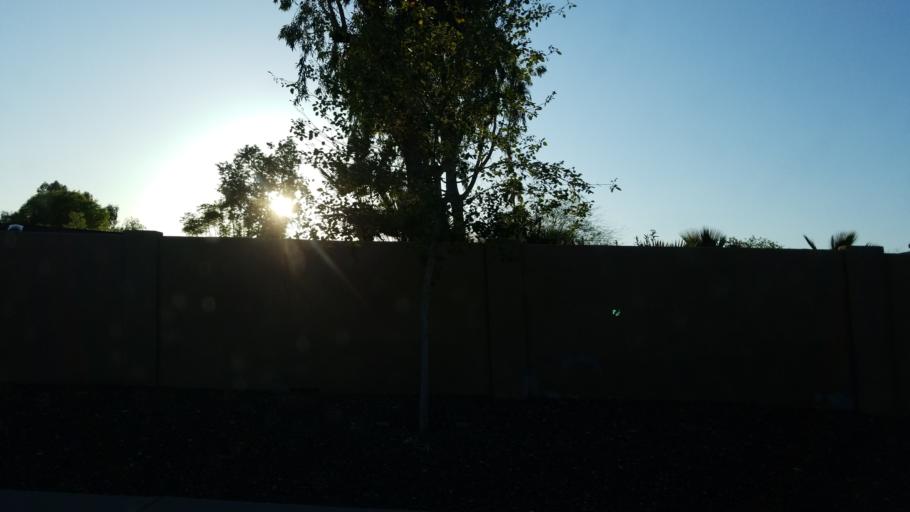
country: US
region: Arizona
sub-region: Maricopa County
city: Paradise Valley
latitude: 33.5782
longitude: -111.9175
